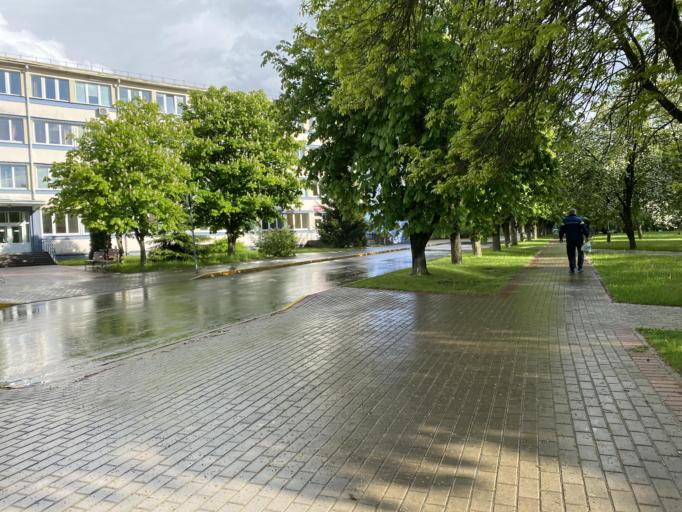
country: BY
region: Minsk
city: Lyasny
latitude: 54.0045
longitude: 27.6864
